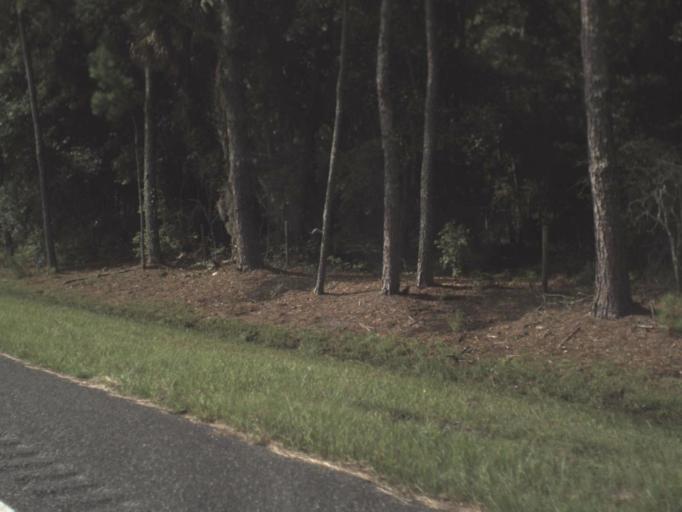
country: US
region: Florida
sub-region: Alachua County
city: Gainesville
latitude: 29.5182
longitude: -82.2974
